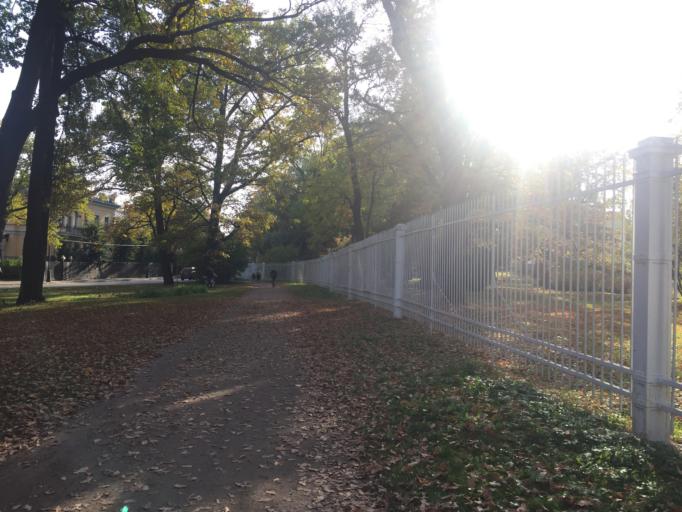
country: RU
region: St.-Petersburg
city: Pushkin
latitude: 59.7225
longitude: 30.3956
